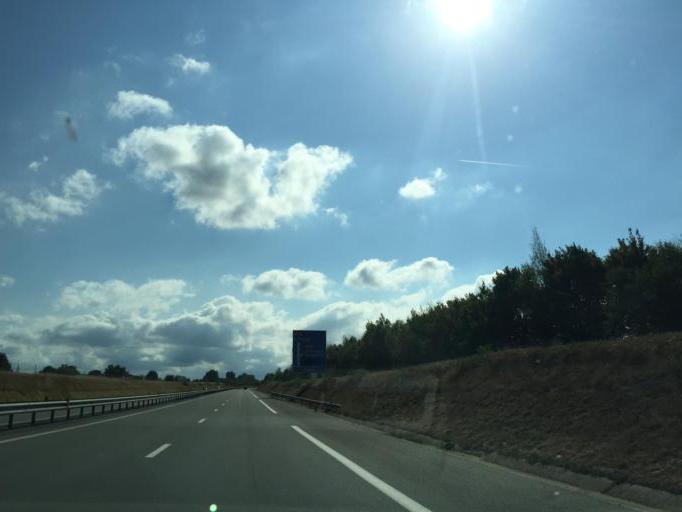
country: FR
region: Rhone-Alpes
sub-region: Departement de la Loire
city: Balbigny
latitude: 45.8298
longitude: 4.1491
